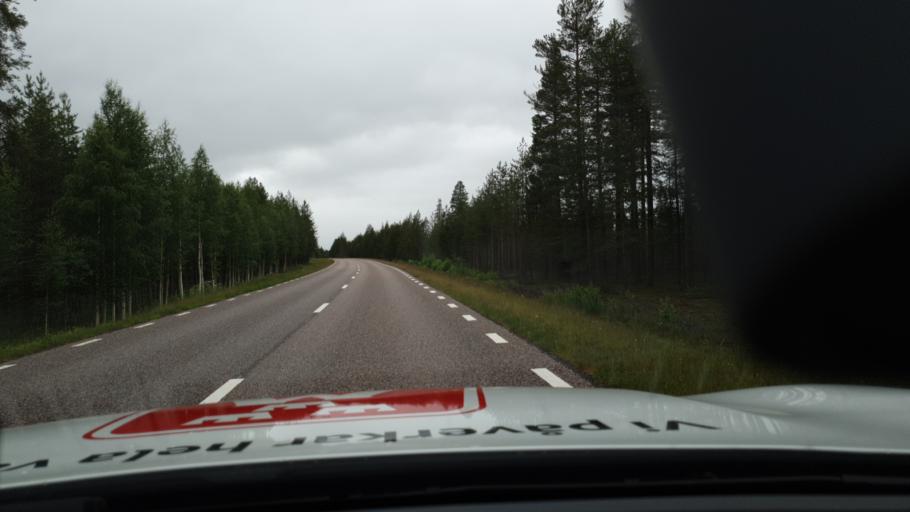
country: FI
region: Lapland
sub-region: Tunturi-Lappi
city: Kolari
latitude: 67.0359
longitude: 23.7074
